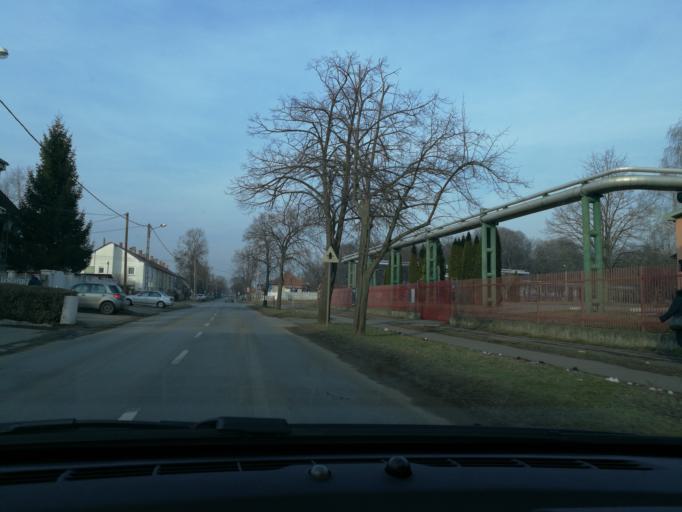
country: HU
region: Szabolcs-Szatmar-Bereg
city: Nyiregyhaza
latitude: 47.9485
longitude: 21.6944
